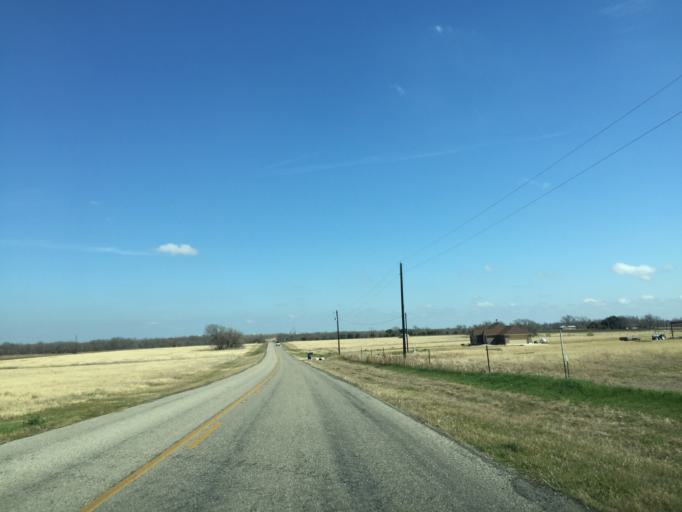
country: US
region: Texas
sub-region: Williamson County
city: Granger
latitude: 30.7543
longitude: -97.5142
